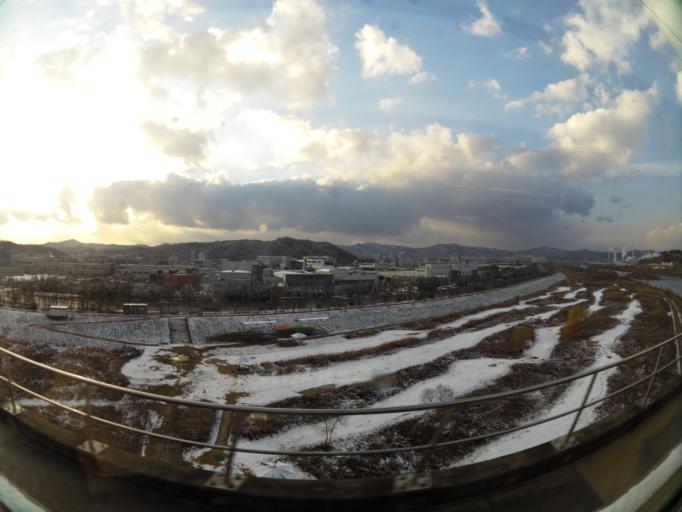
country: KR
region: Daejeon
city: Songgang-dong
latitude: 36.4183
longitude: 127.4157
